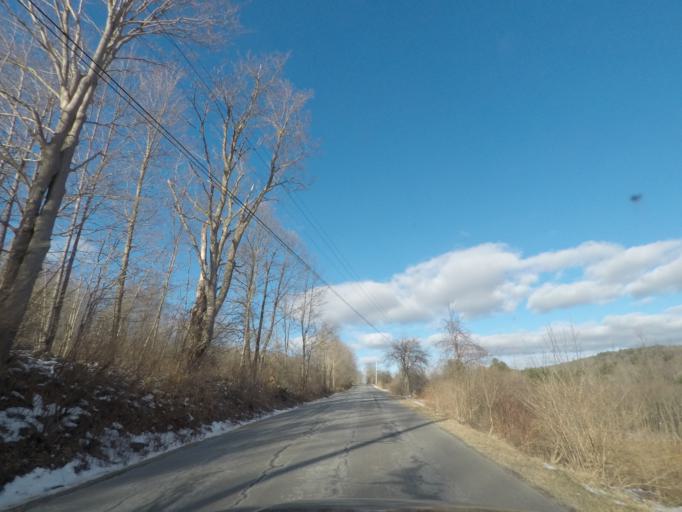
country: US
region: New York
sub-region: Rensselaer County
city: Nassau
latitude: 42.5448
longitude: -73.5287
